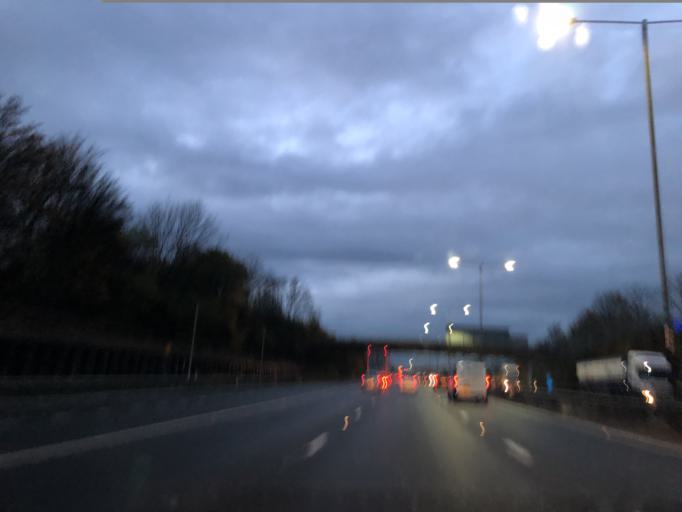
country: GB
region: England
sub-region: Solihull
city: Chelmsley Wood
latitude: 52.4967
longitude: -1.7368
